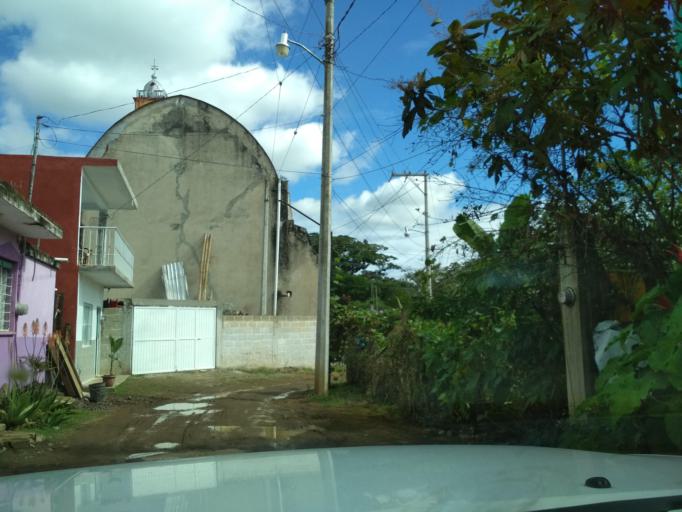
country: MX
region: Veracruz
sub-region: Coatepec
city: Las Lomas
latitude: 19.4374
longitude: -96.9220
